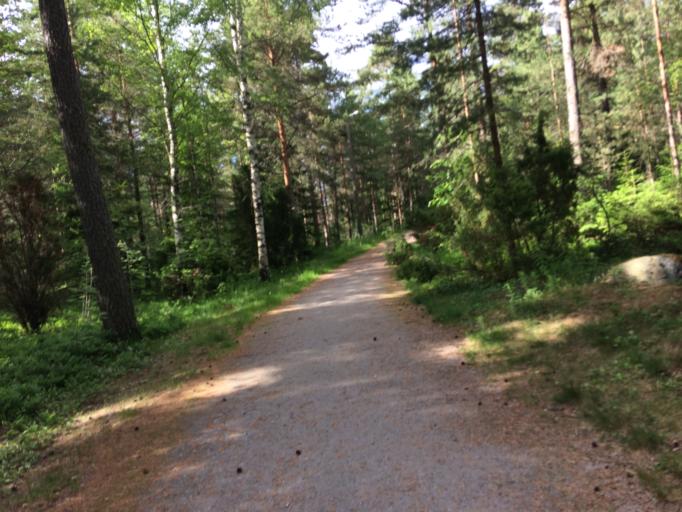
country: FI
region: Varsinais-Suomi
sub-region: Turku
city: Turku
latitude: 60.4704
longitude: 22.3221
